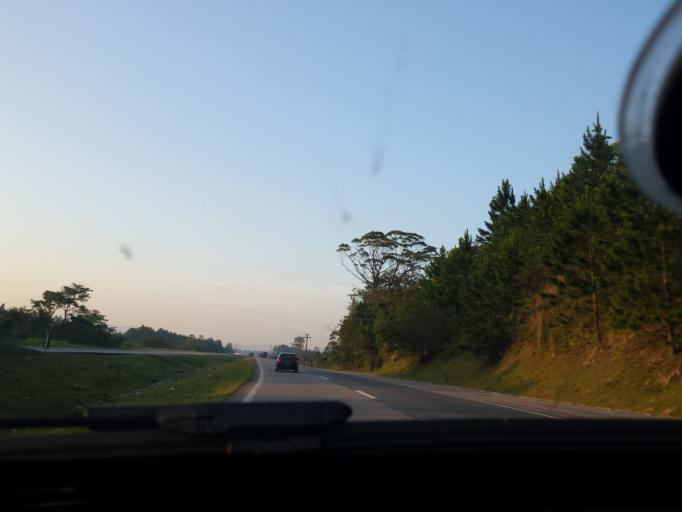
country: BR
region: Santa Catarina
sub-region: Florianopolis
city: Pantano do Sul
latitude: -27.8528
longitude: -48.6418
